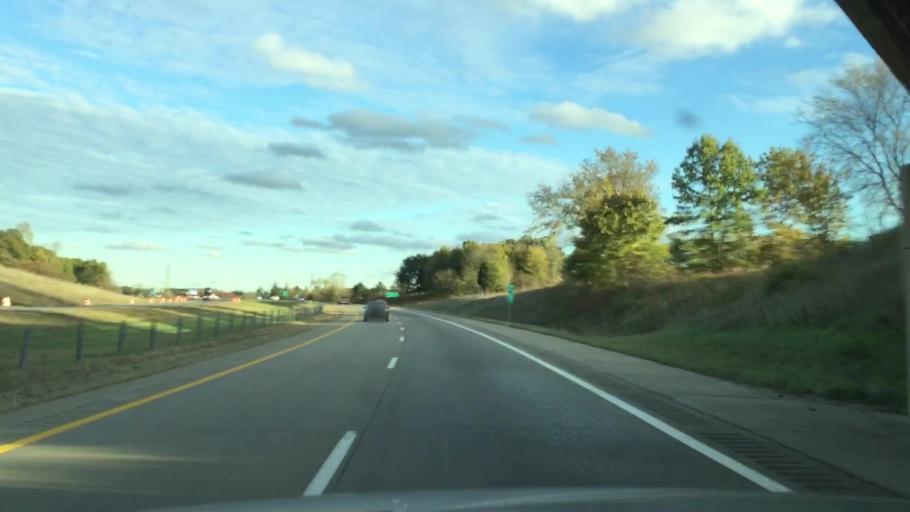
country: US
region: Michigan
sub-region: Calhoun County
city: Albion
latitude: 42.2676
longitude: -84.7760
